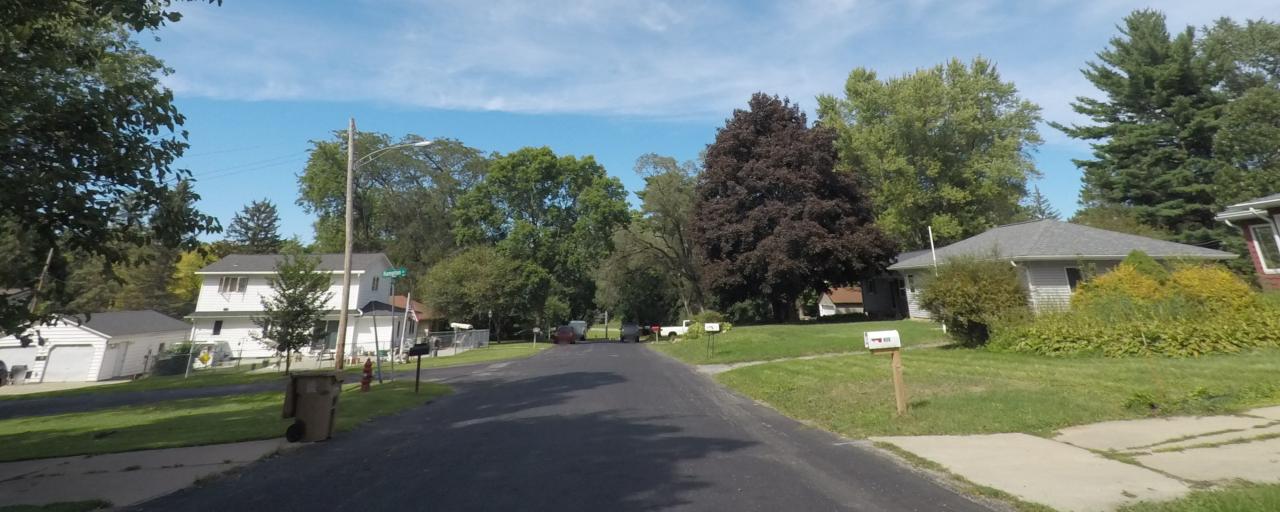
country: US
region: Wisconsin
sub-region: Dane County
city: Shorewood Hills
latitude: 43.0724
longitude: -89.4741
